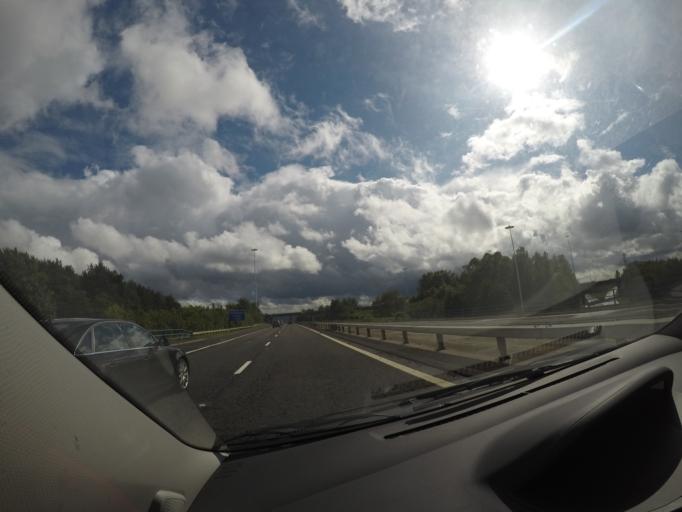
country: GB
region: Scotland
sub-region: South Lanarkshire
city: Uddingston
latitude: 55.8556
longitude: -4.0883
